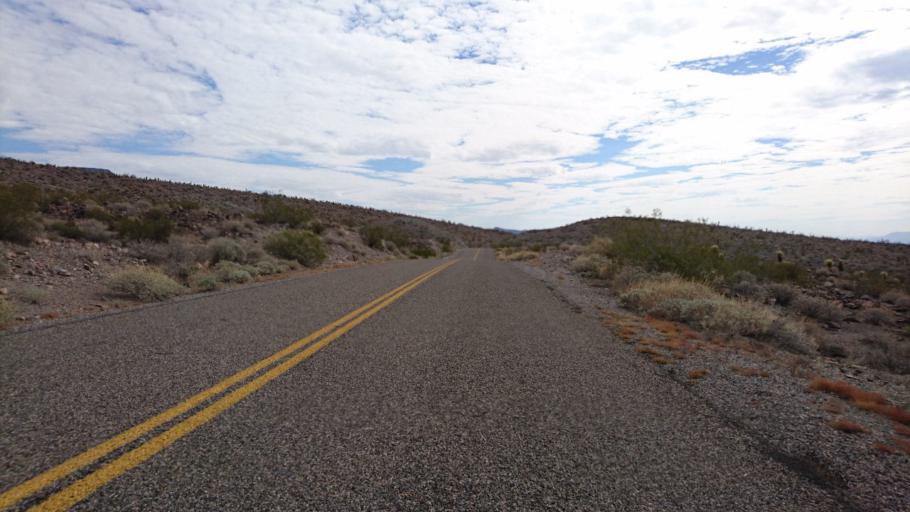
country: US
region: Arizona
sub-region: Mohave County
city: Mohave Valley
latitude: 34.9765
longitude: -114.4195
